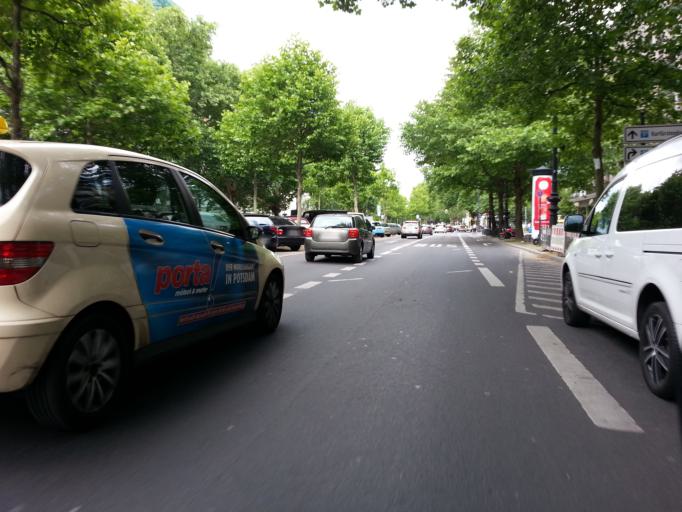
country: DE
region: Berlin
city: Halensee
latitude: 52.5000
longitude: 13.3101
